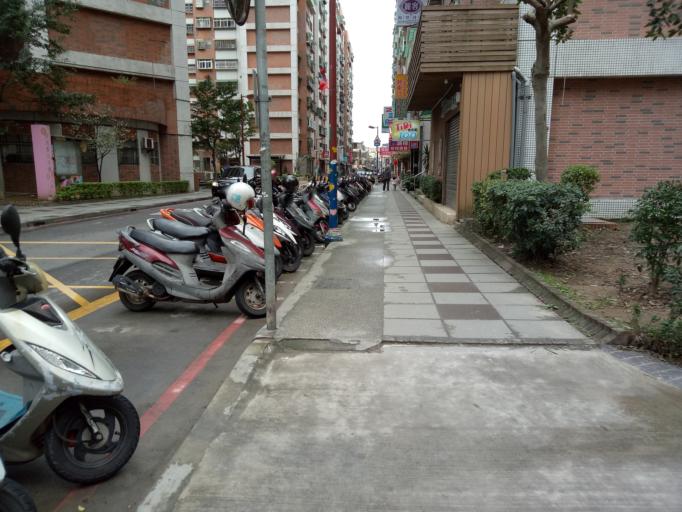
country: TW
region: Taiwan
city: Taoyuan City
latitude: 24.9614
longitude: 121.2969
